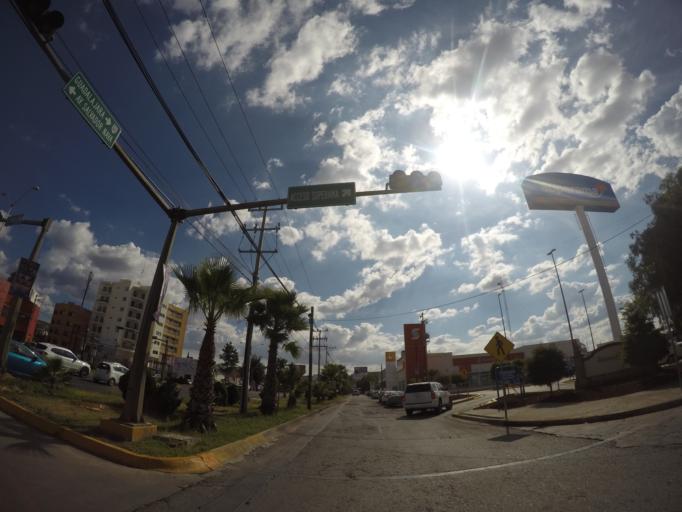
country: MX
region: San Luis Potosi
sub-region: Mexquitic de Carmona
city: Guadalupe Victoria
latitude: 22.1356
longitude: -101.0286
